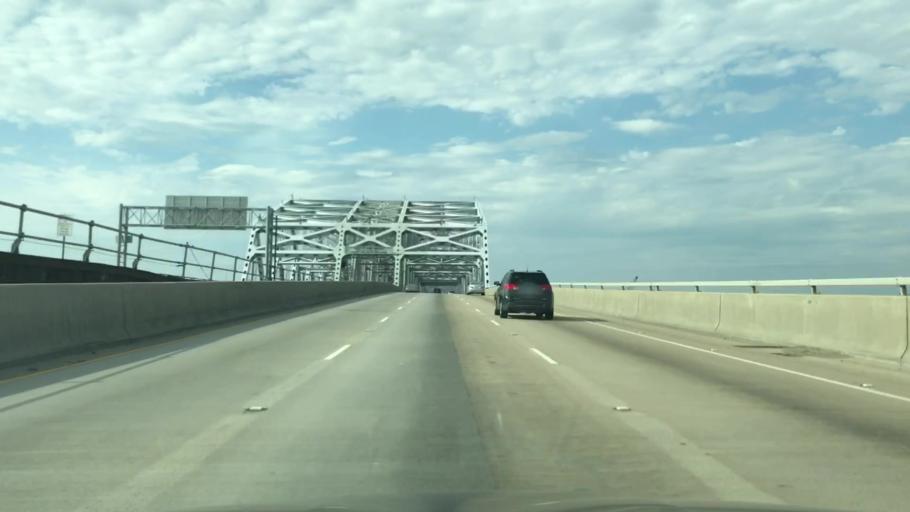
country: US
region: Louisiana
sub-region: Jefferson Parish
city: Bridge City
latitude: 29.9404
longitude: -90.1646
